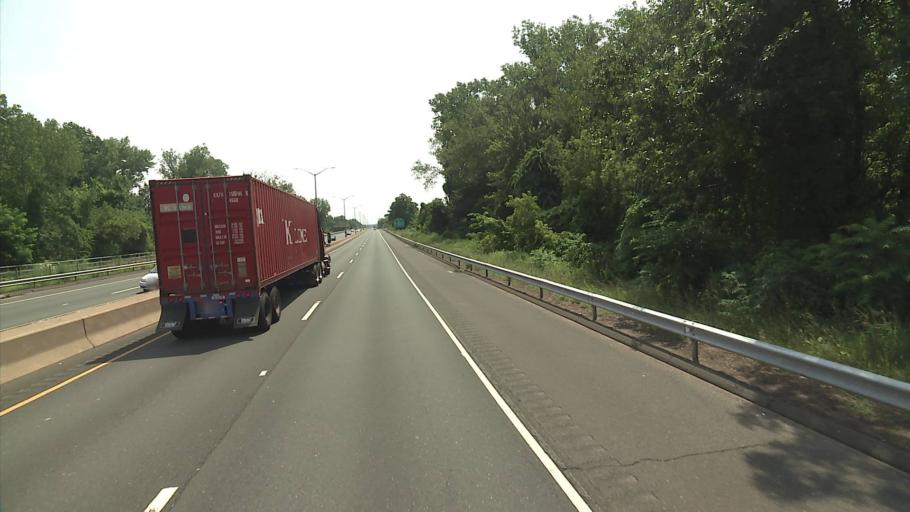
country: US
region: Connecticut
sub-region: Hartford County
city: South Windsor
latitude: 41.8095
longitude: -72.6307
